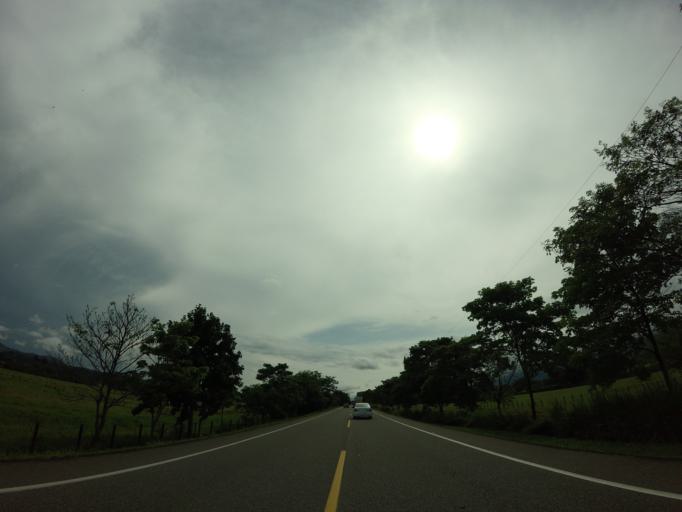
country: CO
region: Caldas
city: La Dorada
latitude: 5.3929
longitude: -74.7026
